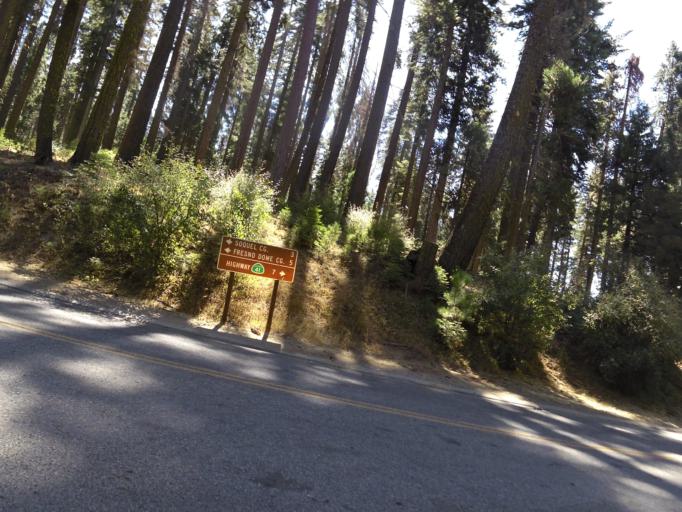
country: US
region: California
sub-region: Madera County
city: Oakhurst
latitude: 37.4120
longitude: -119.5850
